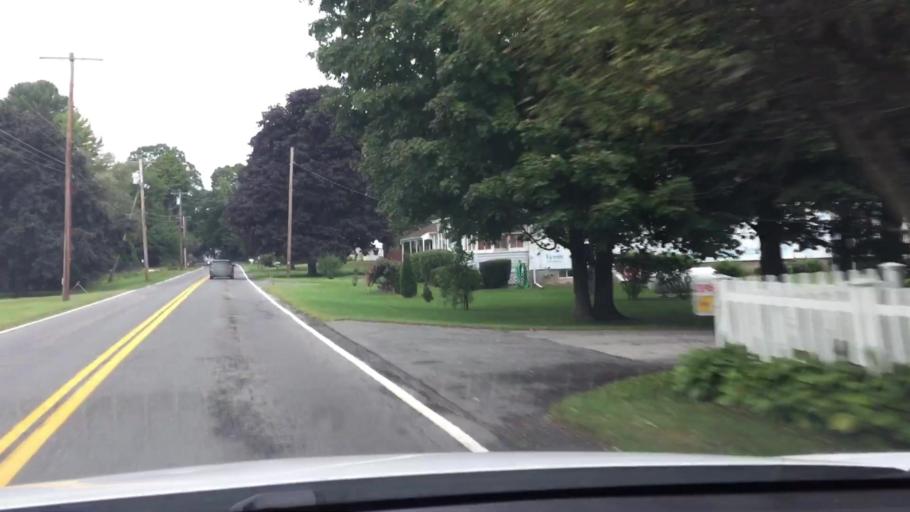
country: US
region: Massachusetts
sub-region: Berkshire County
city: Housatonic
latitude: 42.2550
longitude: -73.3756
